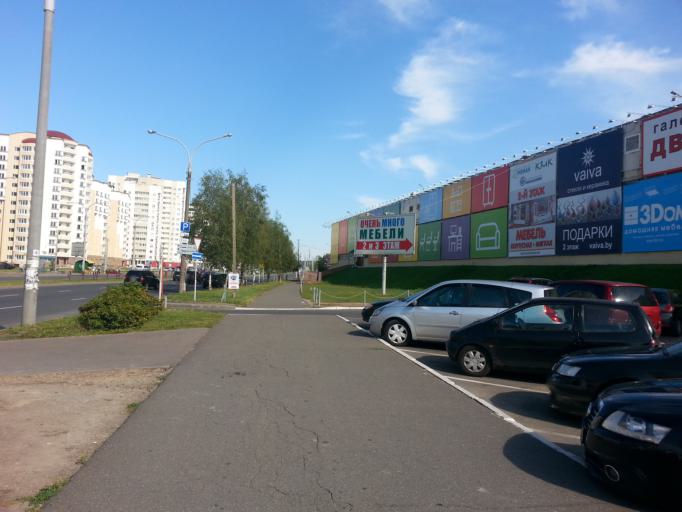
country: BY
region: Minsk
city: Novoye Medvezhino
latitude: 53.9172
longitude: 27.4534
